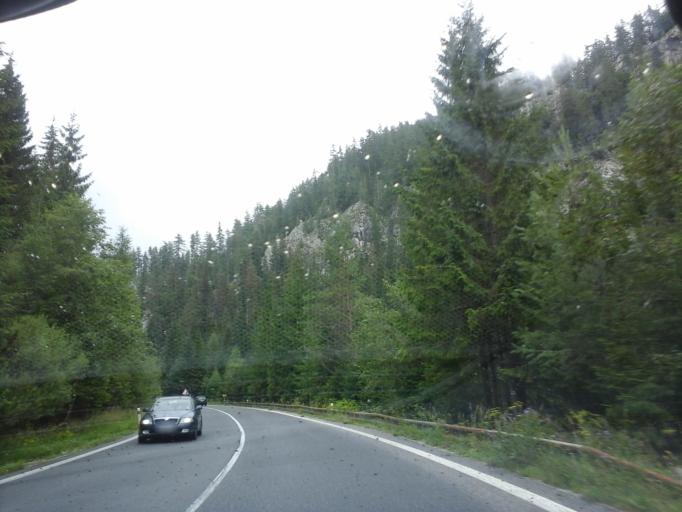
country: SK
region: Kosicky
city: Dobsina
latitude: 48.8826
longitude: 20.3184
